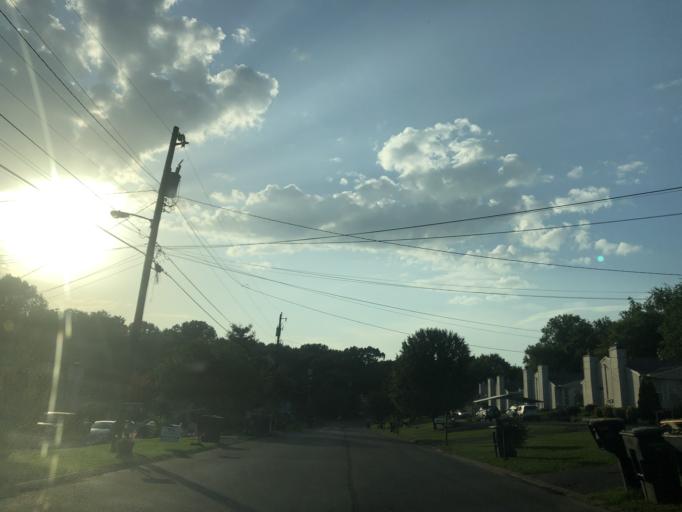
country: US
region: Tennessee
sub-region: Davidson County
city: Lakewood
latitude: 36.1433
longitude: -86.6427
